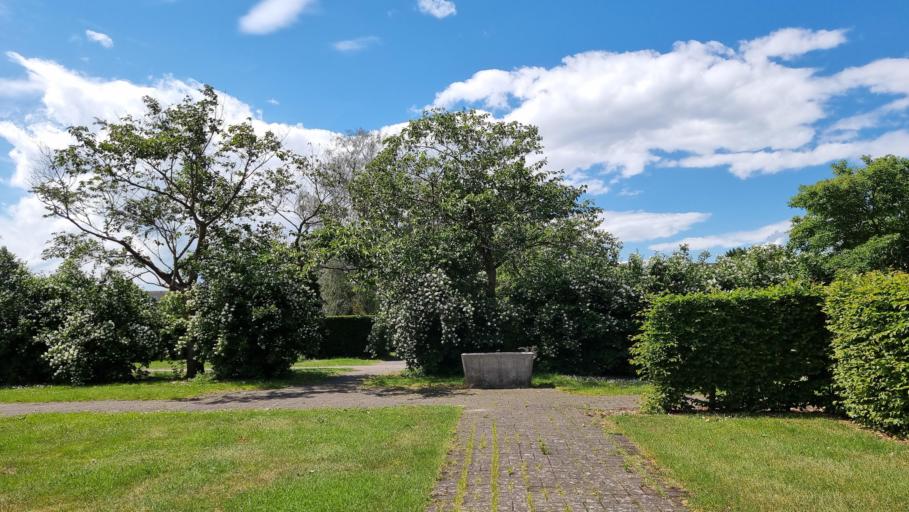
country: DE
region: Lower Saxony
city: Auf der Horst
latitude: 52.4030
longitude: 9.6671
